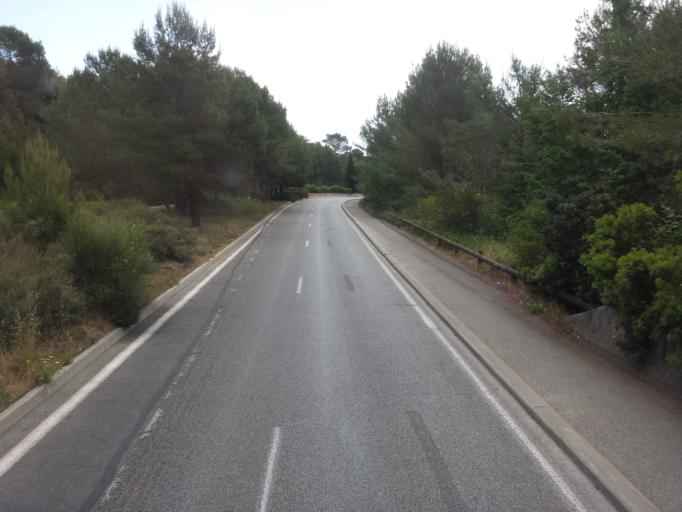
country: FR
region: Provence-Alpes-Cote d'Azur
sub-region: Departement des Alpes-Maritimes
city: Biot
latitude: 43.6116
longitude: 7.0788
